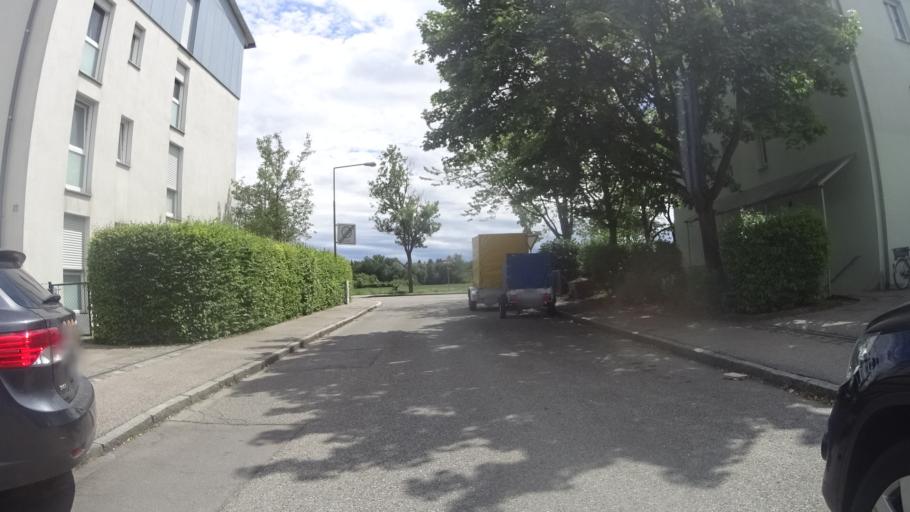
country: DE
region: Bavaria
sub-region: Upper Bavaria
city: Dachau
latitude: 48.2493
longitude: 11.4295
